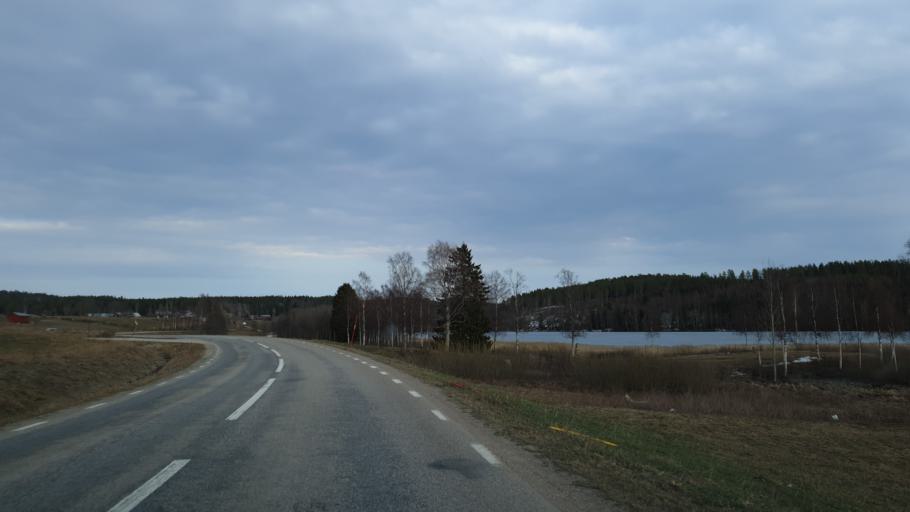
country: SE
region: Gaevleborg
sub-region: Nordanstigs Kommun
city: Bergsjoe
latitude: 61.9791
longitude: 17.2698
